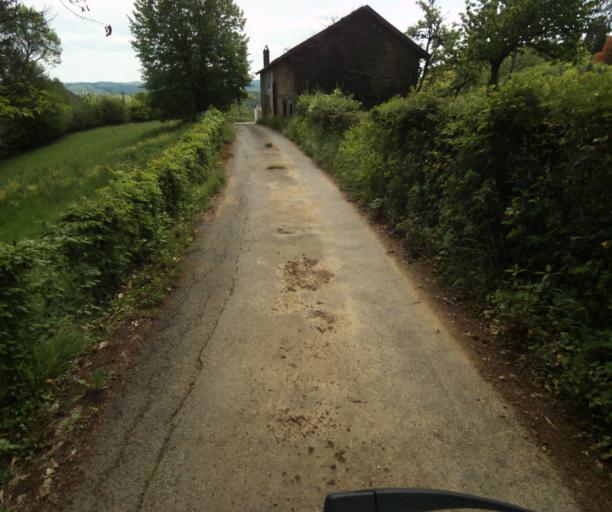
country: FR
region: Limousin
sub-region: Departement de la Correze
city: Tulle
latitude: 45.2706
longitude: 1.7615
